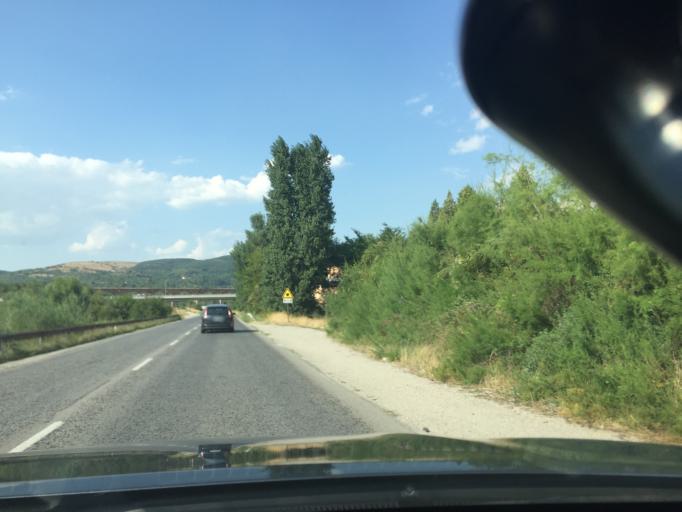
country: BG
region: Kyustendil
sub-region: Obshtina Dupnitsa
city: Dupnitsa
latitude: 42.2503
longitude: 23.0939
